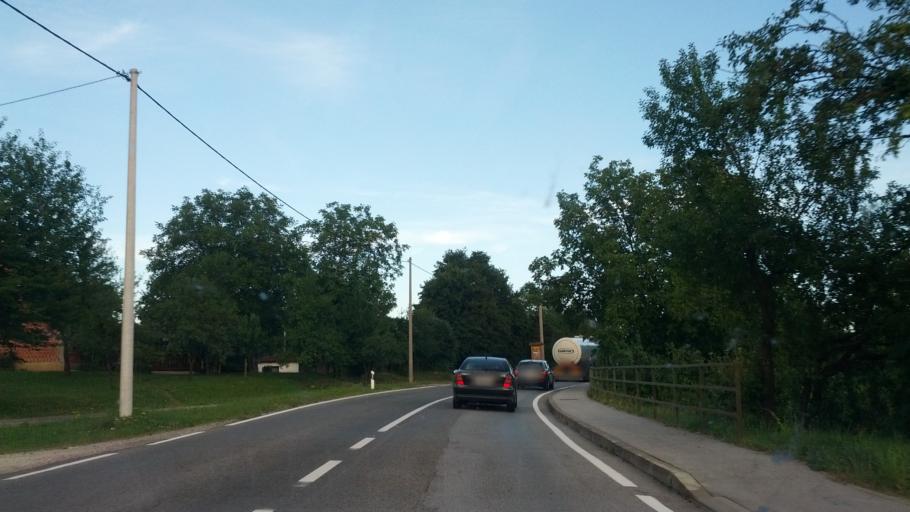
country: HR
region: Licko-Senjska
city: Jezerce
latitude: 44.9590
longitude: 15.6581
